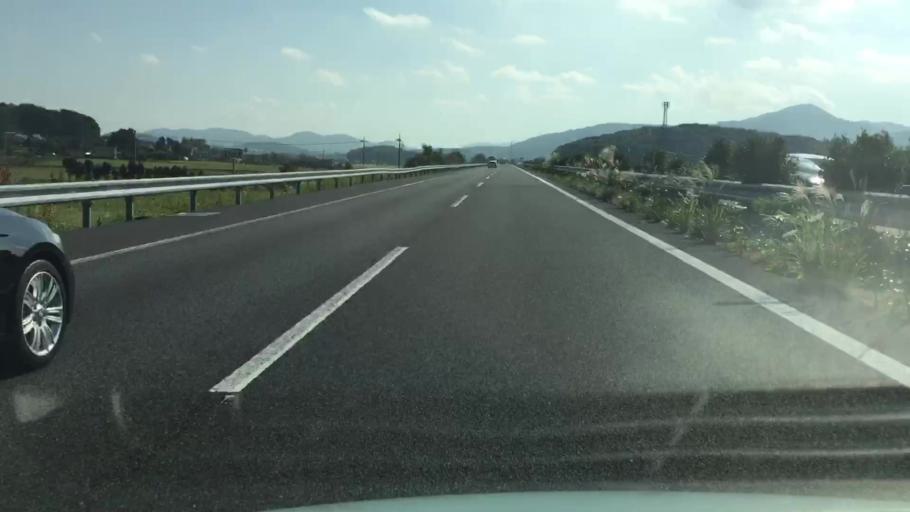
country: JP
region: Ibaraki
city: Iwase
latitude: 36.3638
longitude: 140.0678
